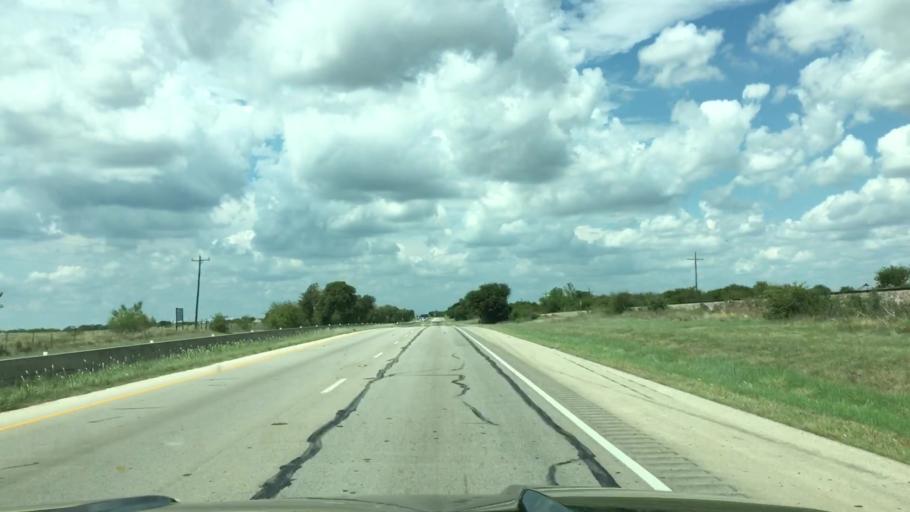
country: US
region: Texas
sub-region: Tarrant County
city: Eagle Mountain
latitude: 32.9121
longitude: -97.4058
